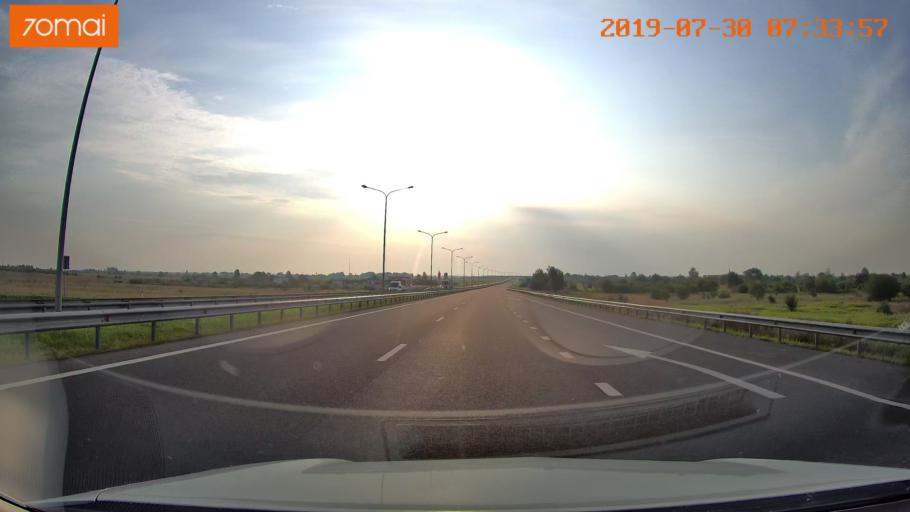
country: RU
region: Kaliningrad
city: Gvardeysk
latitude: 54.6712
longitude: 21.0596
